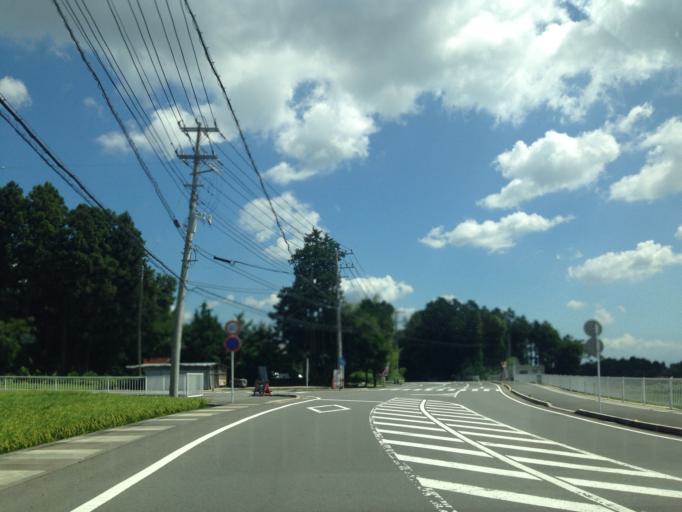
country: JP
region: Shizuoka
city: Gotemba
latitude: 35.2161
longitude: 138.8962
